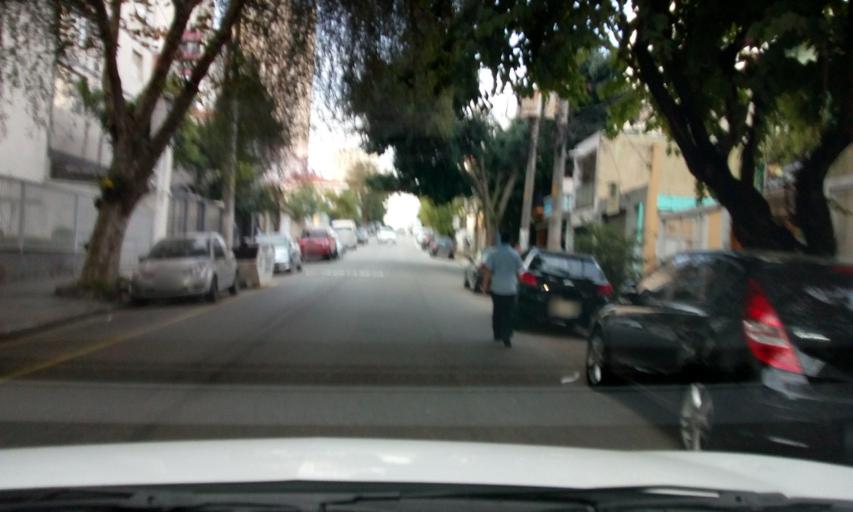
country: BR
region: Sao Paulo
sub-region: Sao Paulo
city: Sao Paulo
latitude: -23.5428
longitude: -46.6867
